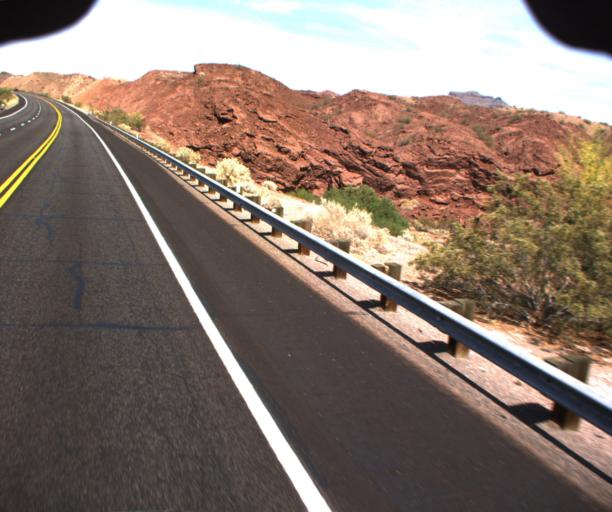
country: US
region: Arizona
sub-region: La Paz County
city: Cienega Springs
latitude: 34.2248
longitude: -114.1847
